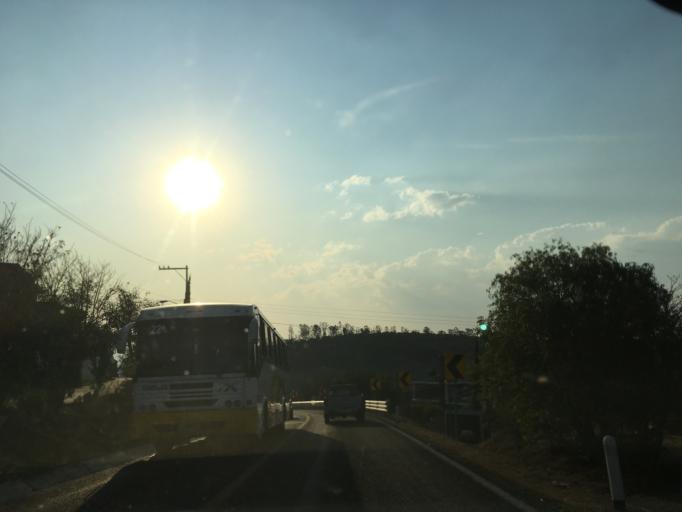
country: MX
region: Michoacan
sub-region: Morelia
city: Fraccionamiento Mision del Valle
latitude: 19.7381
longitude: -101.0970
